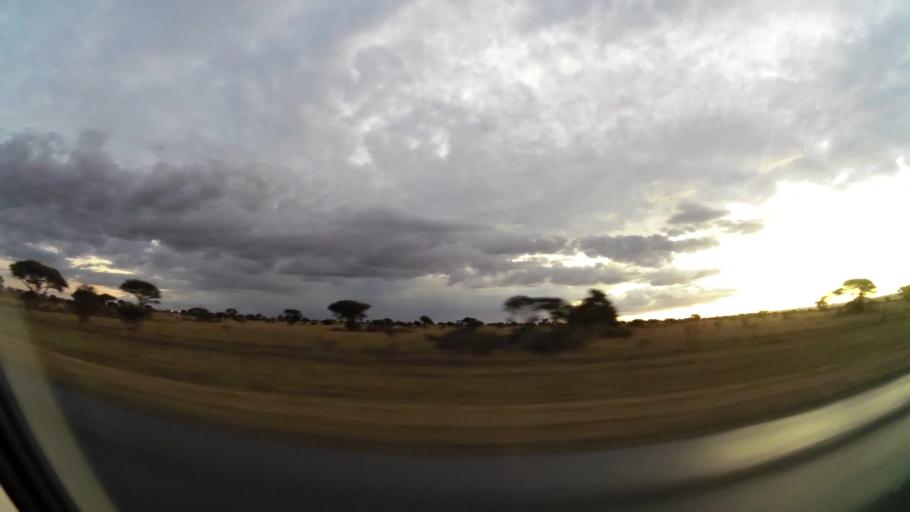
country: ZA
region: Limpopo
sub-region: Capricorn District Municipality
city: Polokwane
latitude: -23.8371
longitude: 29.4268
